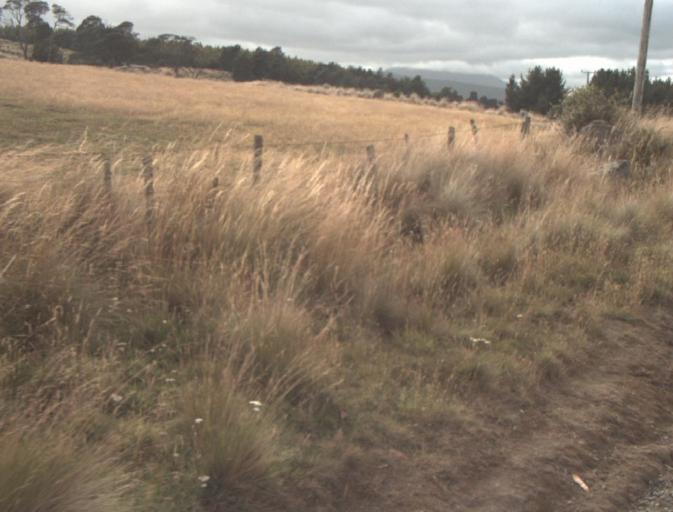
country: AU
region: Tasmania
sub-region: Dorset
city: Scottsdale
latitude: -41.3558
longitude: 147.4562
